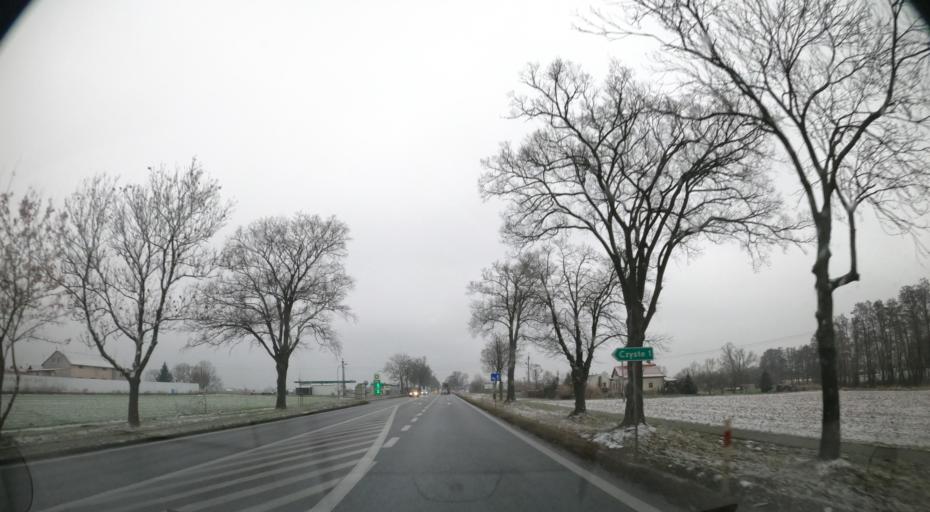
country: PL
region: Masovian Voivodeship
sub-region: Powiat sochaczewski
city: Sochaczew
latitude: 52.2251
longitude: 20.2858
